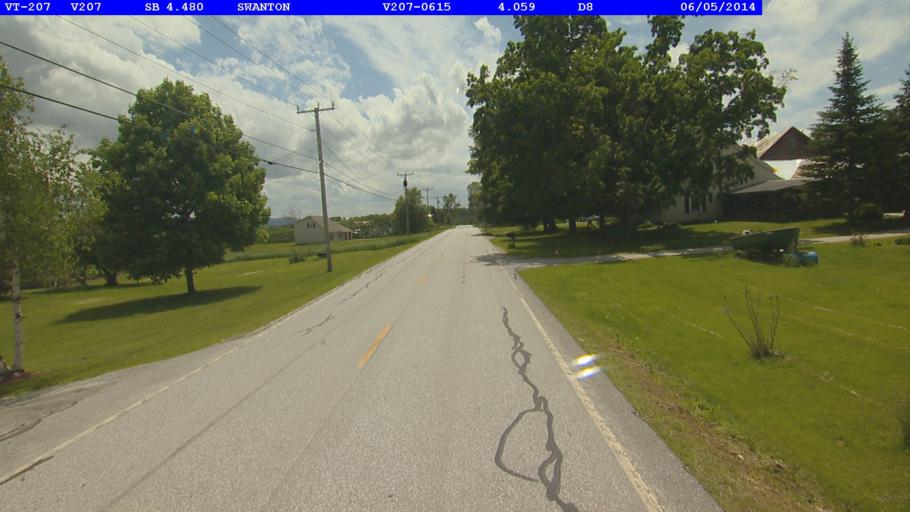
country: US
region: Vermont
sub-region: Franklin County
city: Swanton
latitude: 44.9024
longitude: -73.0652
